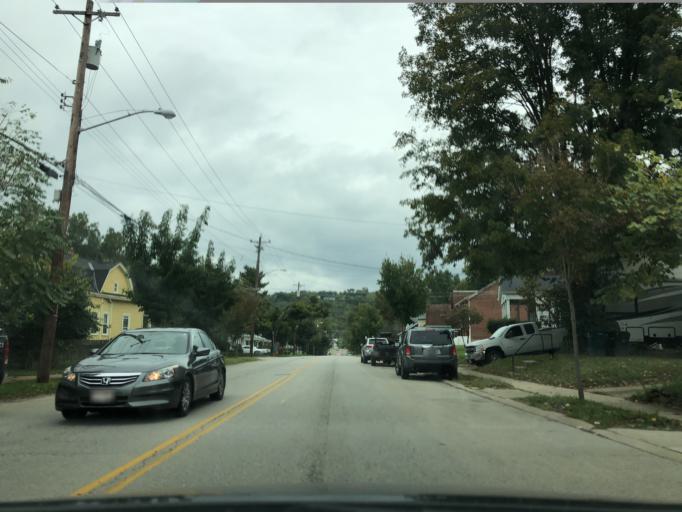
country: US
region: Ohio
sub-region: Hamilton County
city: Mariemont
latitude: 39.1549
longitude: -84.3807
